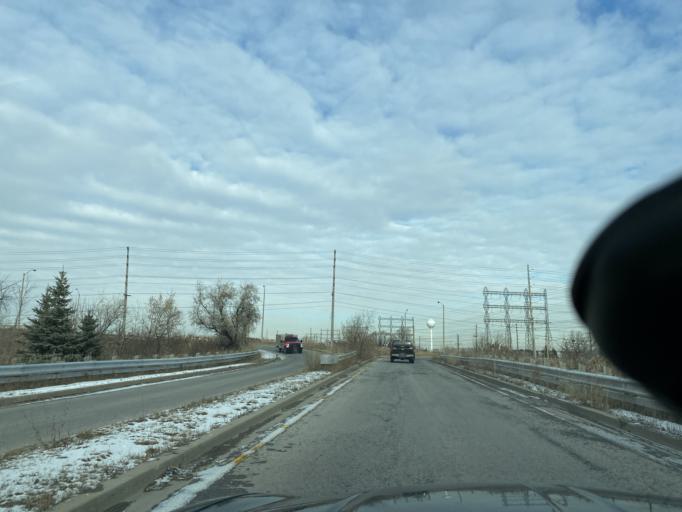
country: CA
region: Ontario
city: Etobicoke
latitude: 43.6882
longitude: -79.5805
